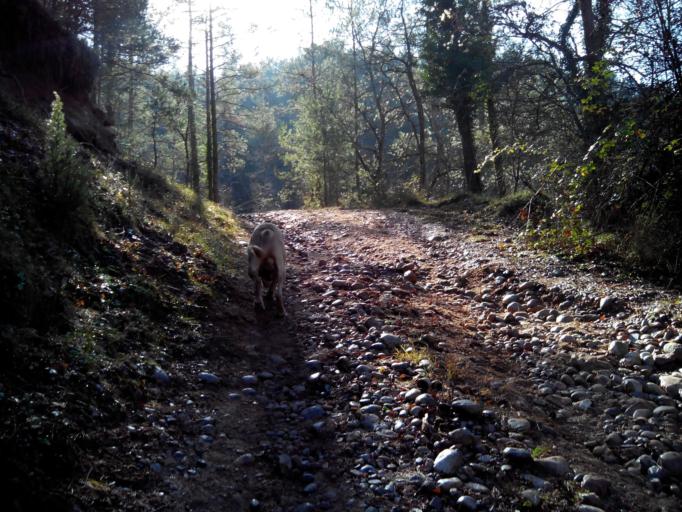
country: ES
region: Catalonia
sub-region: Provincia de Barcelona
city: Vilada
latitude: 42.1047
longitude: 1.9456
